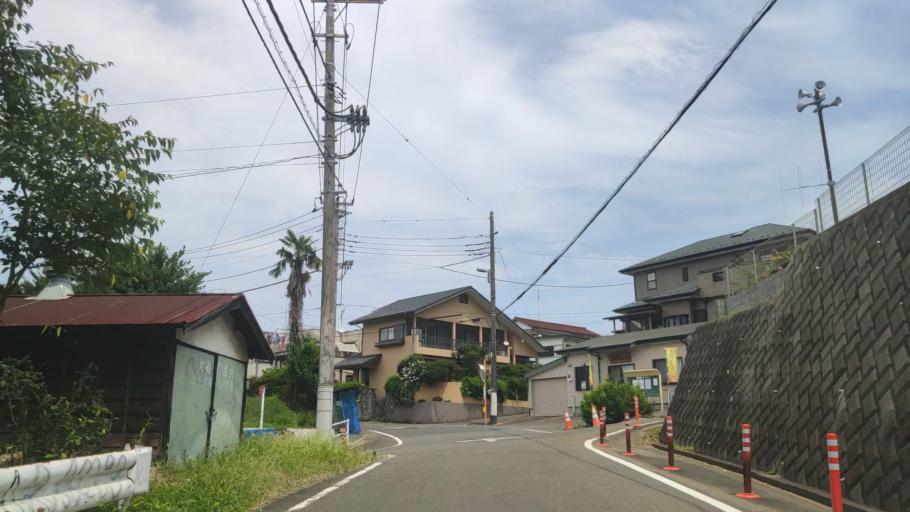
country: JP
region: Kanagawa
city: Atsugi
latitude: 35.4403
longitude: 139.3955
